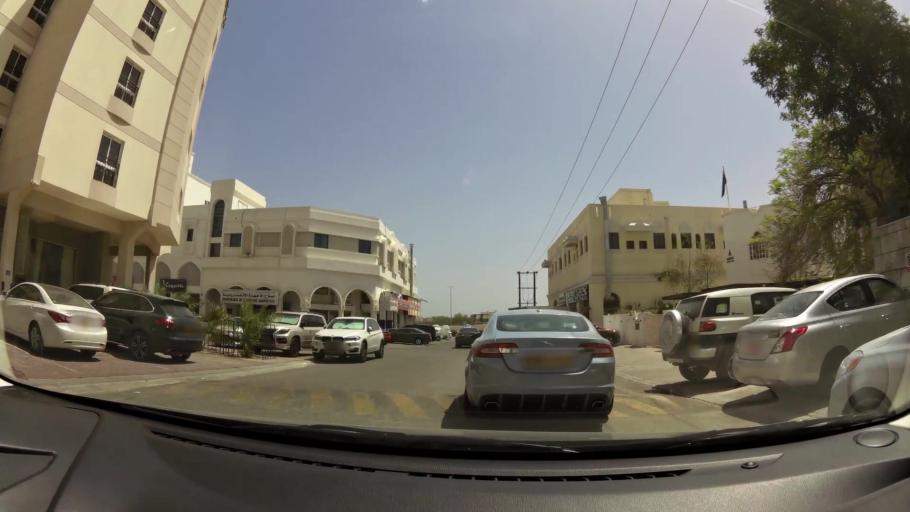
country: OM
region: Muhafazat Masqat
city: Bawshar
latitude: 23.5924
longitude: 58.4571
